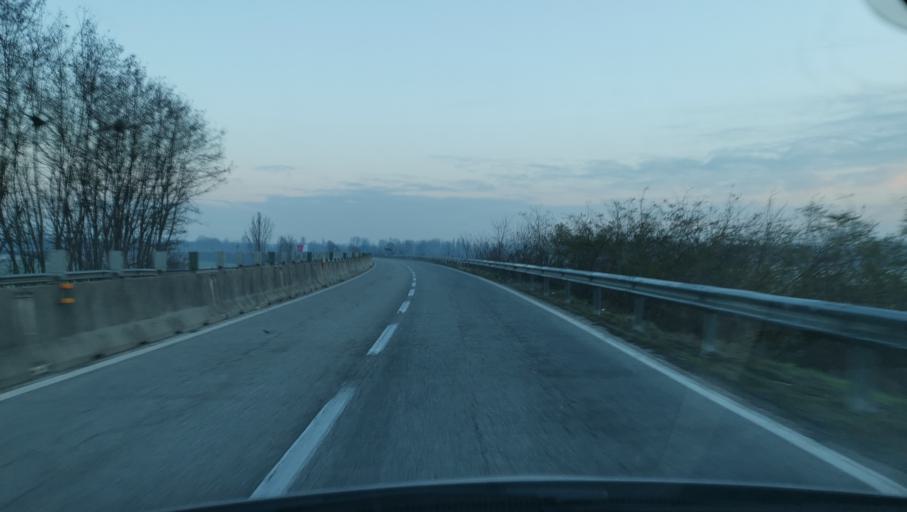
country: IT
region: Piedmont
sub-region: Provincia di Torino
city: Brandizzo
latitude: 45.1802
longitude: 7.8579
